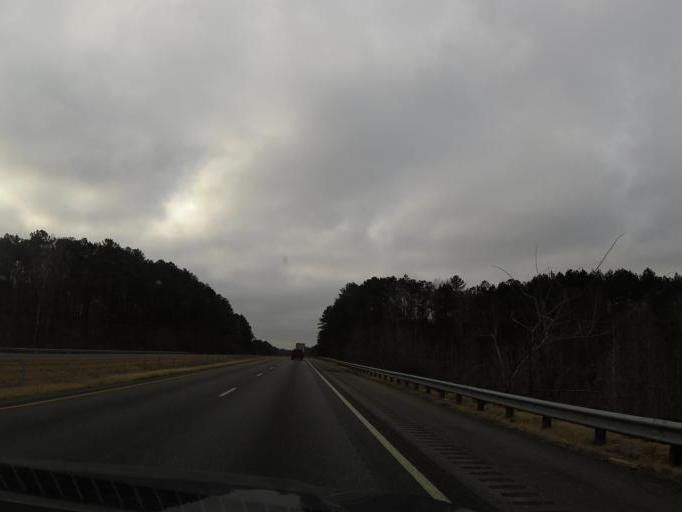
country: US
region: Alabama
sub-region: Shelby County
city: Calera
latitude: 33.0515
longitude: -86.7274
